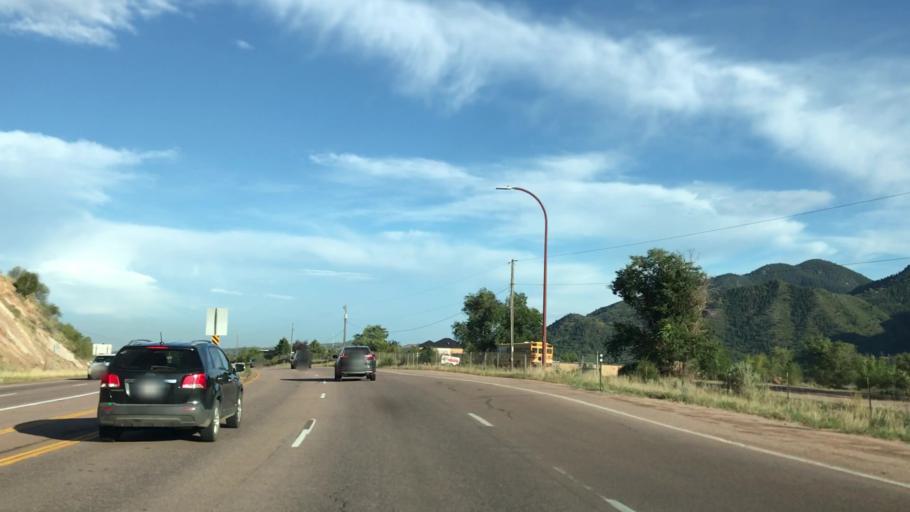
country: US
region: Colorado
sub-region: El Paso County
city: Manitou Springs
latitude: 38.8649
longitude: -104.9207
